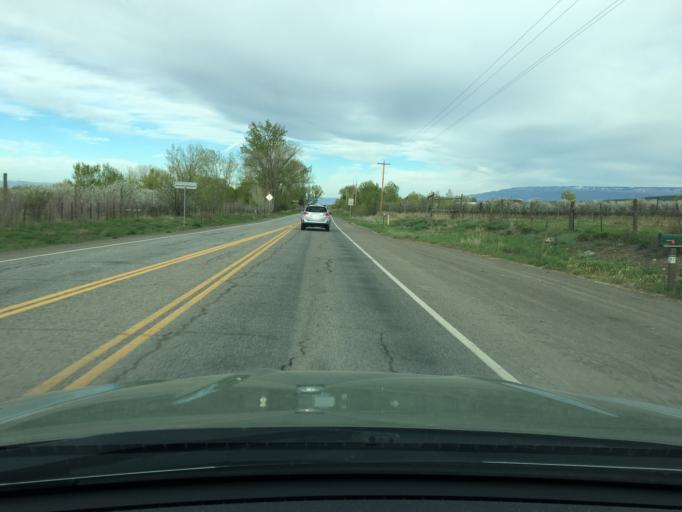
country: US
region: Colorado
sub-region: Delta County
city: Cedaredge
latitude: 38.8005
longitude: -107.7834
